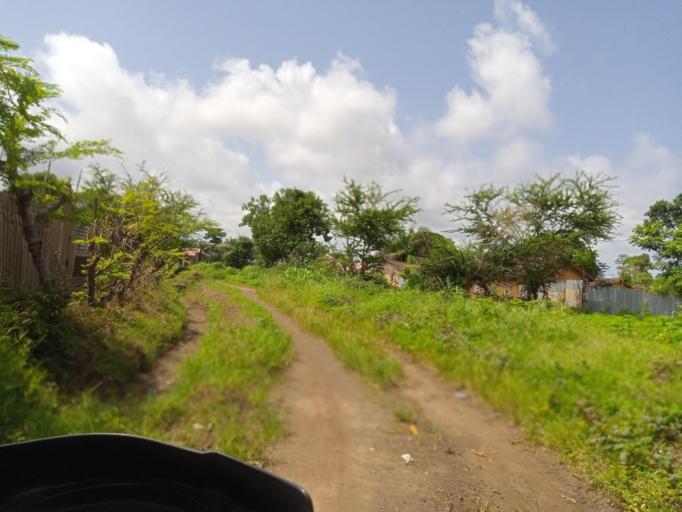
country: SL
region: Northern Province
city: Tintafor
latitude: 8.6247
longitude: -13.2096
